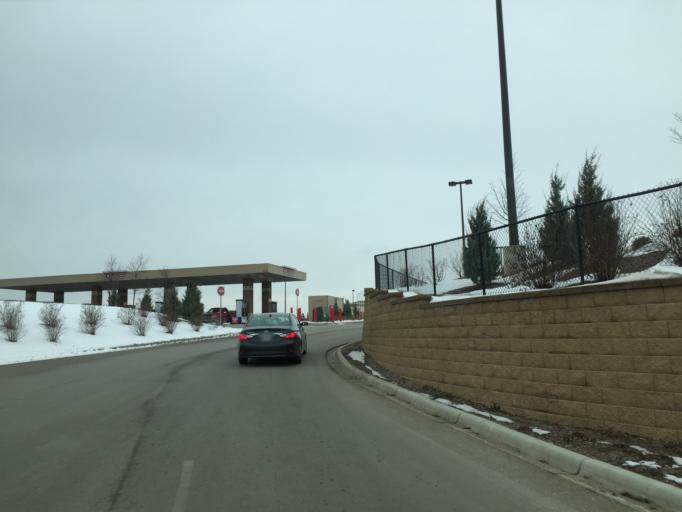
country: US
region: Minnesota
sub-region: Olmsted County
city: Rochester
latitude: 44.0459
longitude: -92.5162
